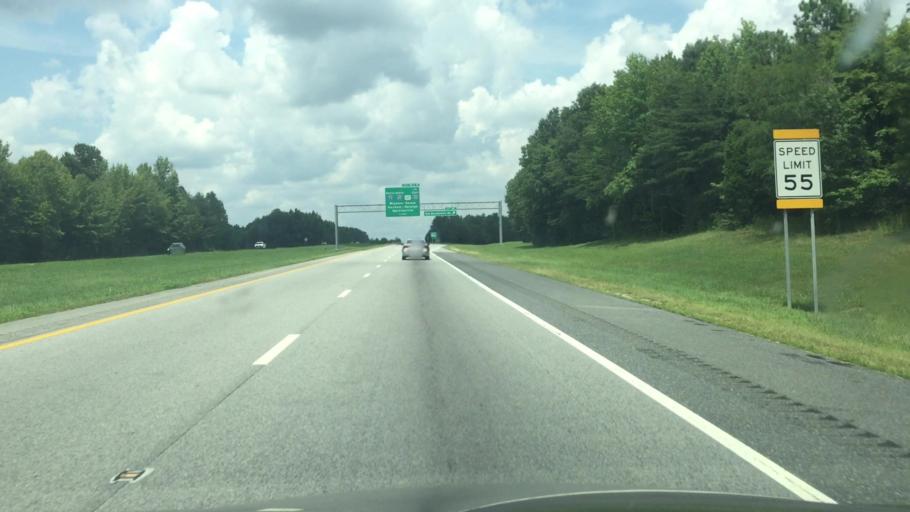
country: US
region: North Carolina
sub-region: Guilford County
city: Pleasant Garden
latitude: 35.9821
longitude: -79.8233
